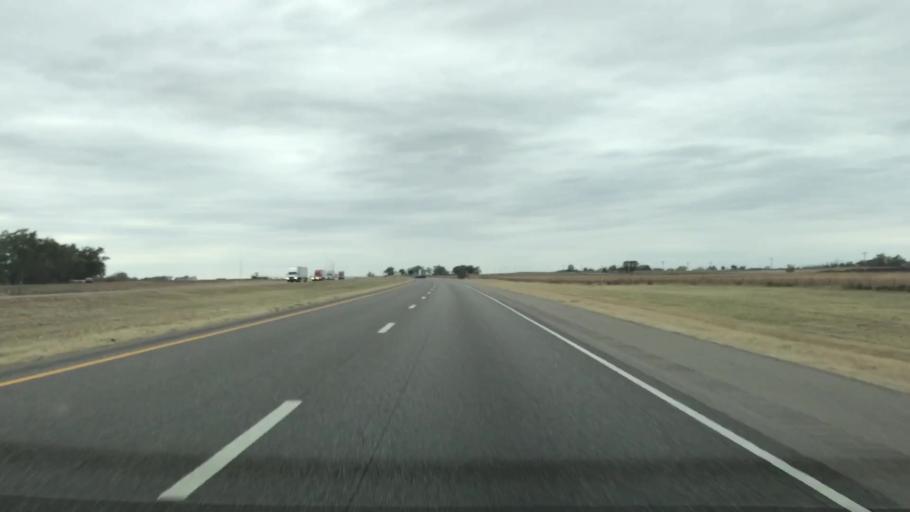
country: US
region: Oklahoma
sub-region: Beckham County
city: Erick
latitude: 35.2320
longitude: -99.9507
